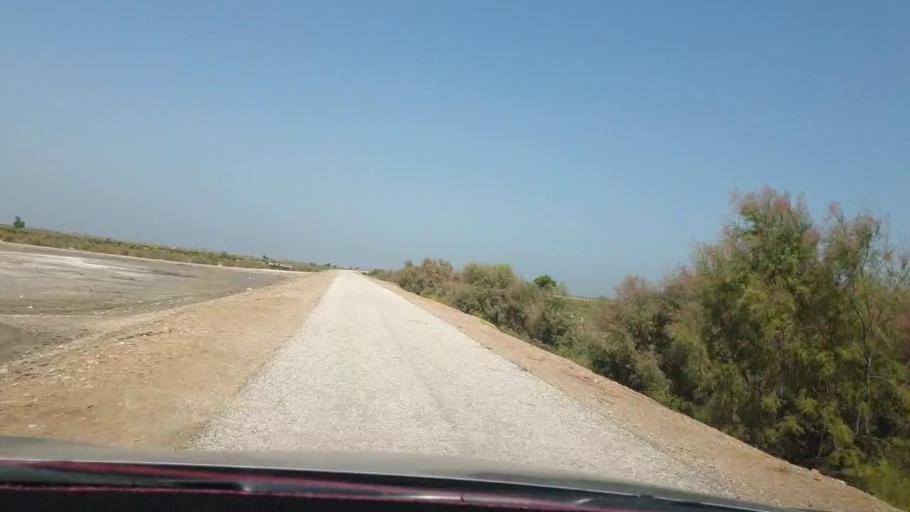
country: PK
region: Sindh
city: Warah
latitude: 27.5268
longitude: 67.7113
